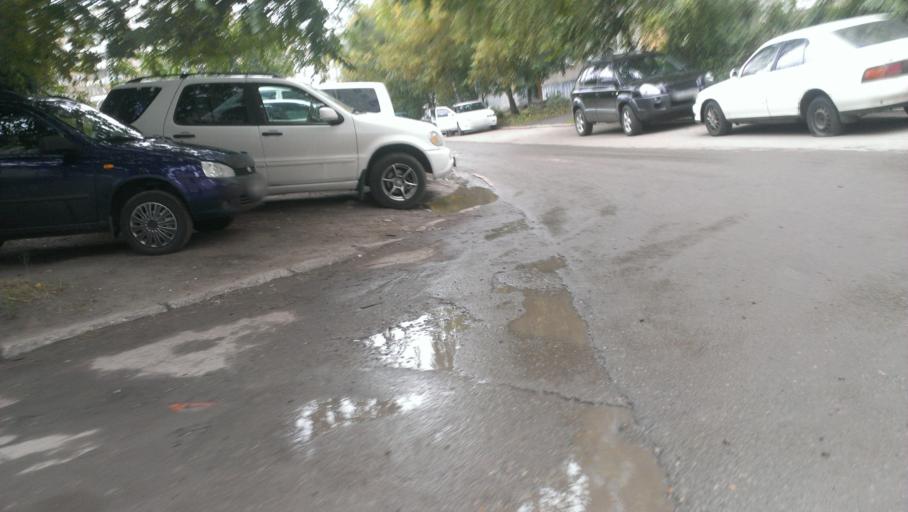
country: RU
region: Altai Krai
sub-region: Gorod Barnaulskiy
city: Barnaul
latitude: 53.3717
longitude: 83.6890
